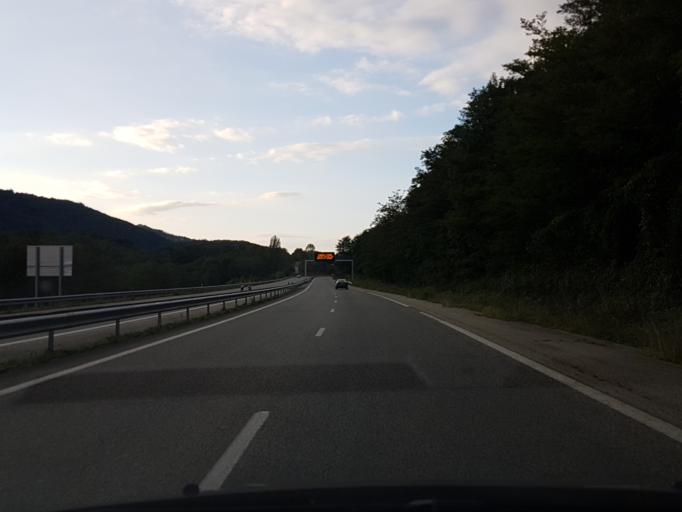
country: FR
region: Midi-Pyrenees
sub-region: Departement de l'Ariege
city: Montgaillard
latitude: 42.9292
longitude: 1.6316
